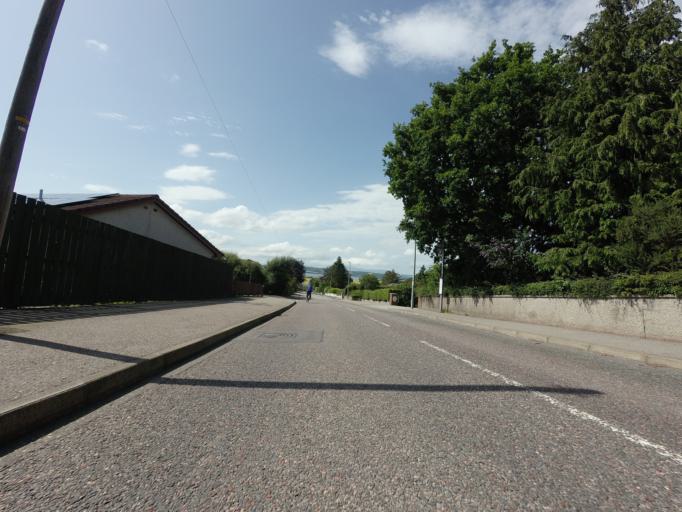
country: GB
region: Scotland
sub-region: Highland
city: Fortrose
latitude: 57.4951
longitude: -4.1154
